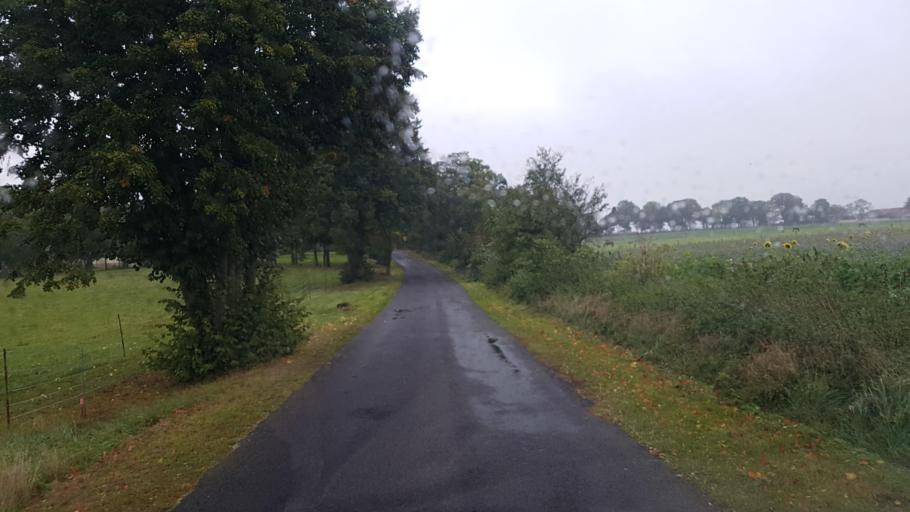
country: DE
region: Brandenburg
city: Furstenwalde
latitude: 52.4003
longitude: 14.0612
